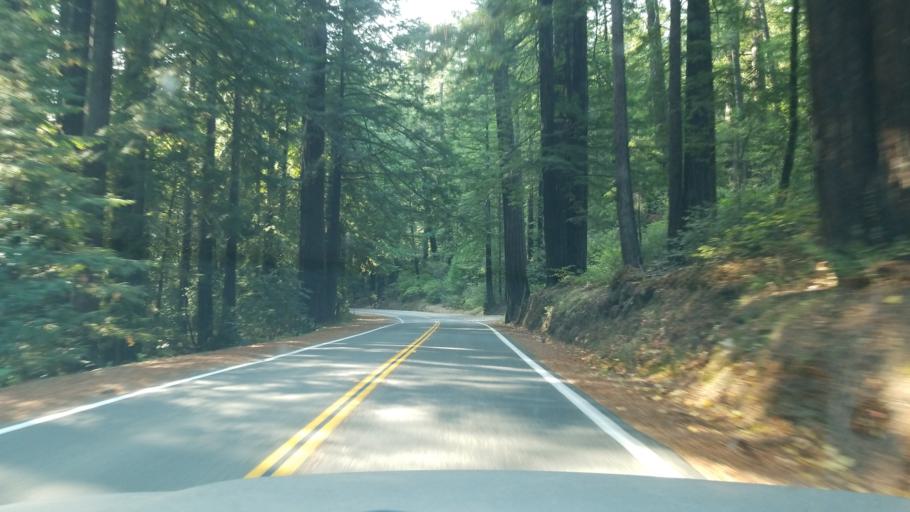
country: US
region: California
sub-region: Humboldt County
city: Redway
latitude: 40.2579
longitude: -123.8345
